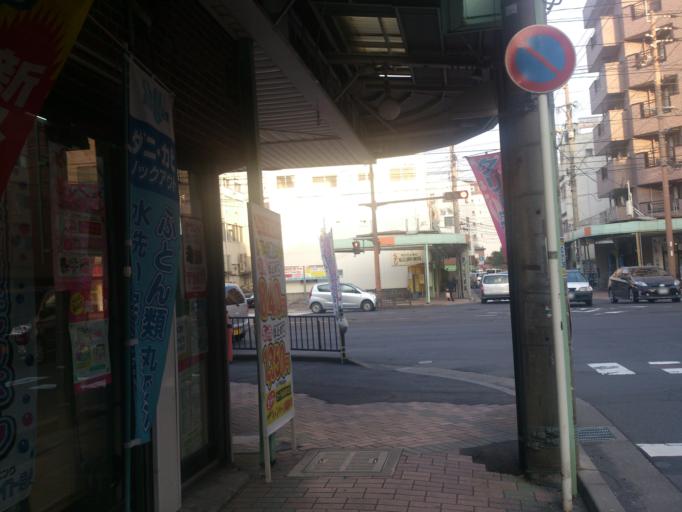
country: JP
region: Kagoshima
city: Kagoshima-shi
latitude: 31.5807
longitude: 130.5427
